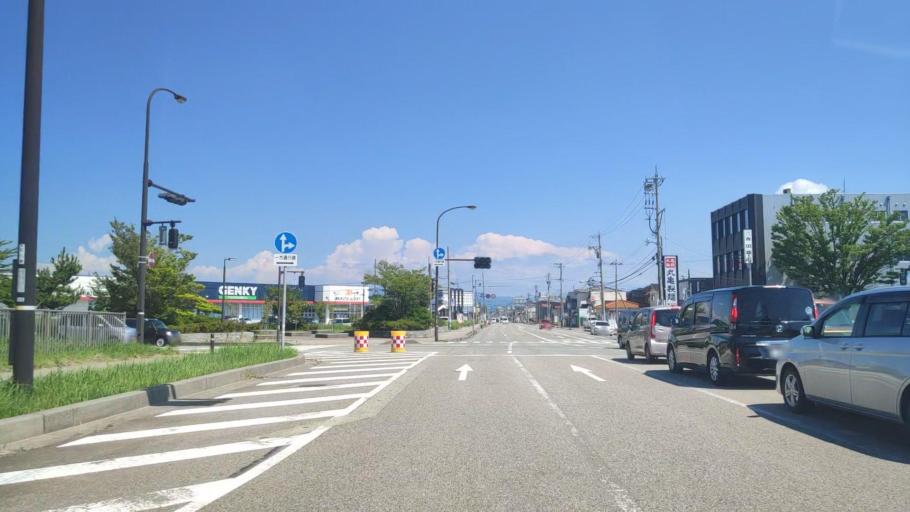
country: JP
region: Ishikawa
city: Kanazawa-shi
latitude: 36.5950
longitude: 136.6056
